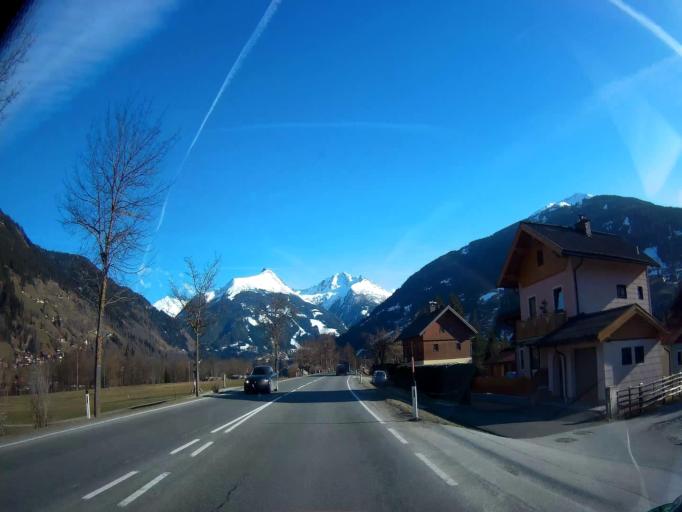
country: AT
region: Salzburg
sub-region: Politischer Bezirk Sankt Johann im Pongau
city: Bad Hofgastein
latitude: 47.1537
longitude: 13.1117
